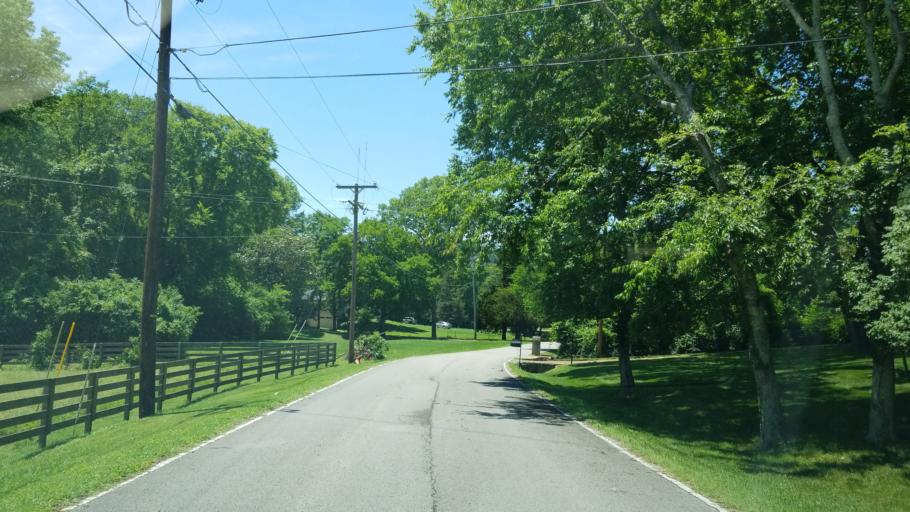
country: US
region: Tennessee
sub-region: Williamson County
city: Brentwood
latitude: 36.0478
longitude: -86.8100
